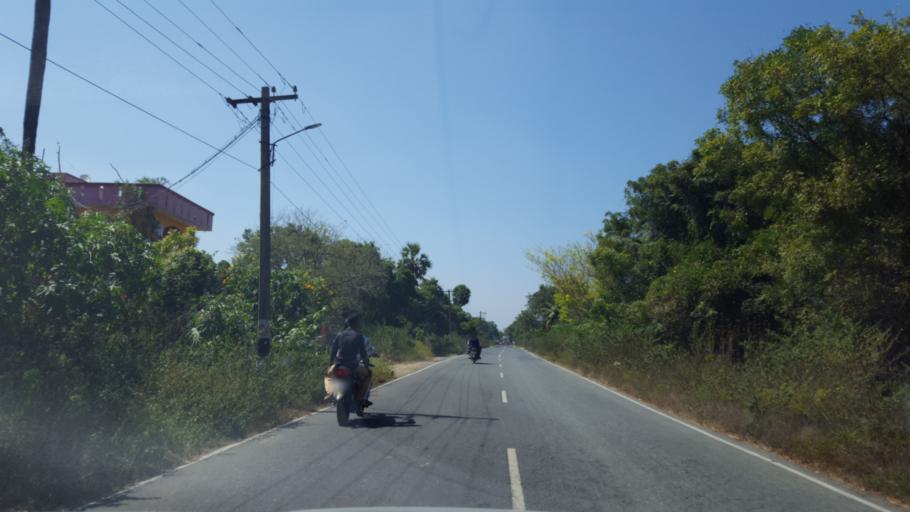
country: IN
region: Tamil Nadu
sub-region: Kancheepuram
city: Wallajahbad
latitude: 12.7658
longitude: 79.9060
